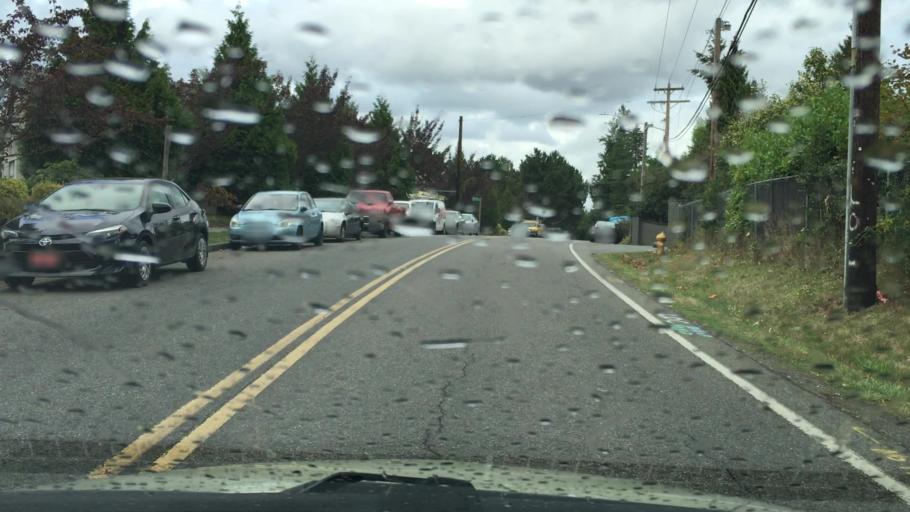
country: US
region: Washington
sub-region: Snohomish County
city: Martha Lake
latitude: 47.8837
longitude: -122.2494
